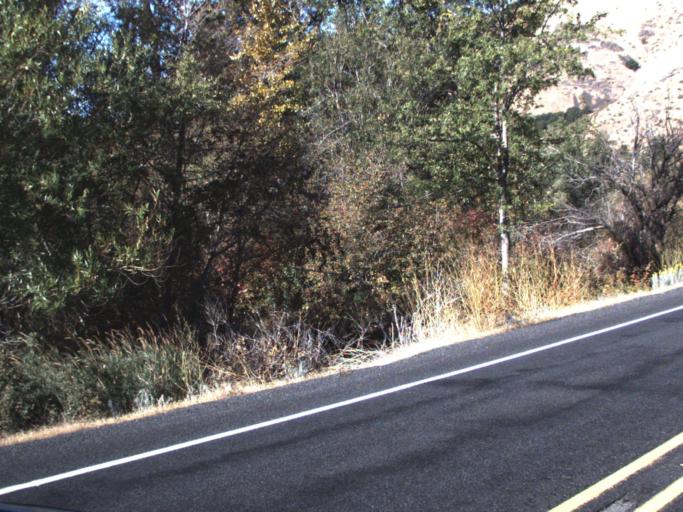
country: US
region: Washington
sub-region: Yakima County
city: Tieton
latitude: 46.7207
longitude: -120.8385
